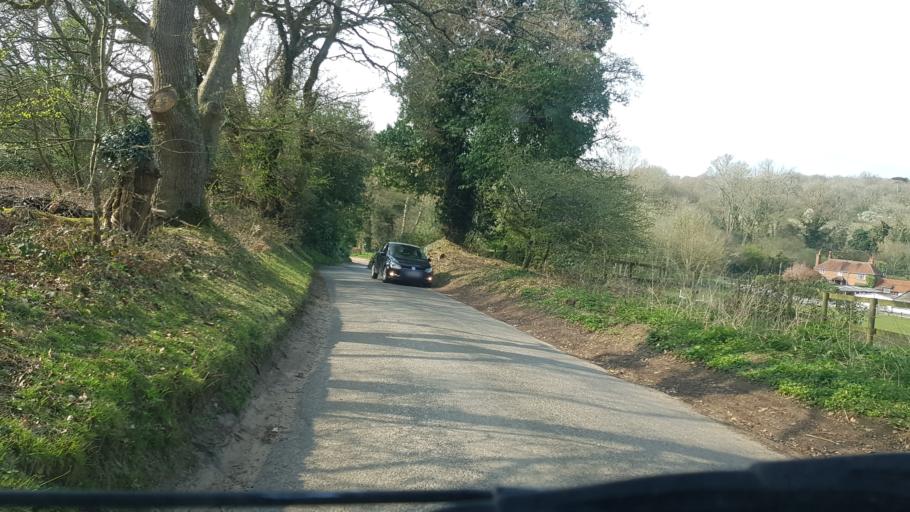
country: GB
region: England
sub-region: Surrey
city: Chilworth
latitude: 51.2269
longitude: -0.5192
